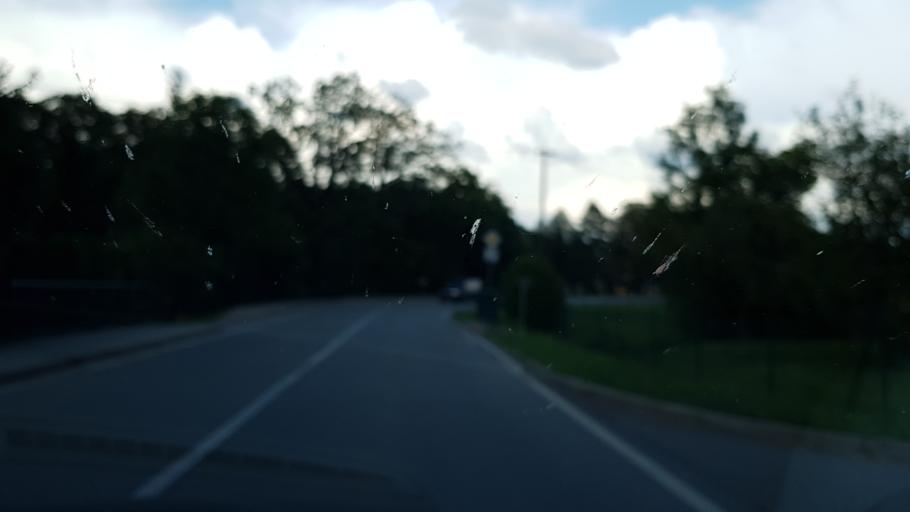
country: CZ
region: Pardubicky
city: Zamberk
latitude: 50.0859
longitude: 16.4718
